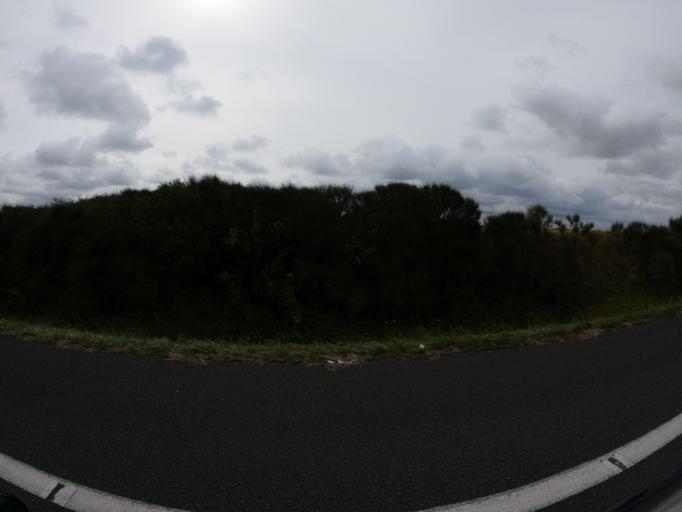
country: FR
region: Centre
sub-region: Departement du Loir-et-Cher
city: Mer
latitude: 47.7226
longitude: 1.4928
